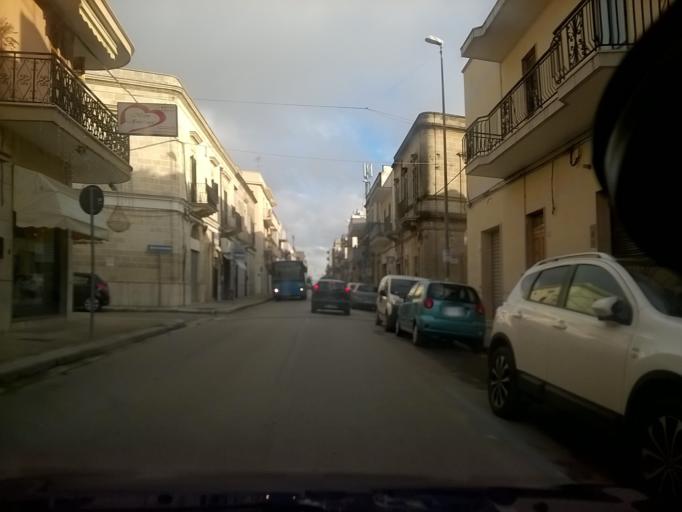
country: IT
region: Apulia
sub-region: Provincia di Brindisi
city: Francavilla Fontana
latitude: 40.5281
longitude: 17.5791
